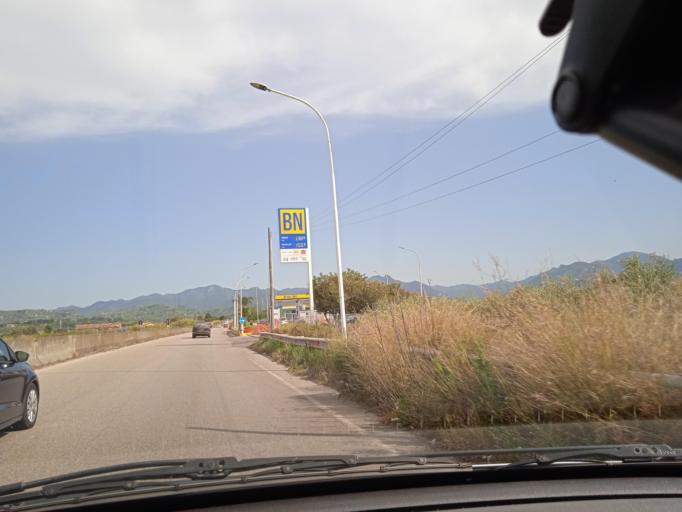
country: IT
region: Sicily
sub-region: Messina
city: Milazzo
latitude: 38.1932
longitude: 15.2582
